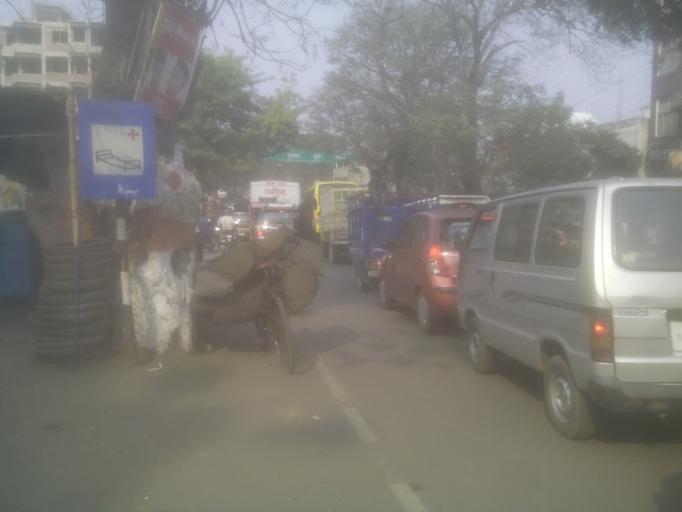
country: IN
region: Jharkhand
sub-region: Dhanbad
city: Dhanbad
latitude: 23.8059
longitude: 86.4313
